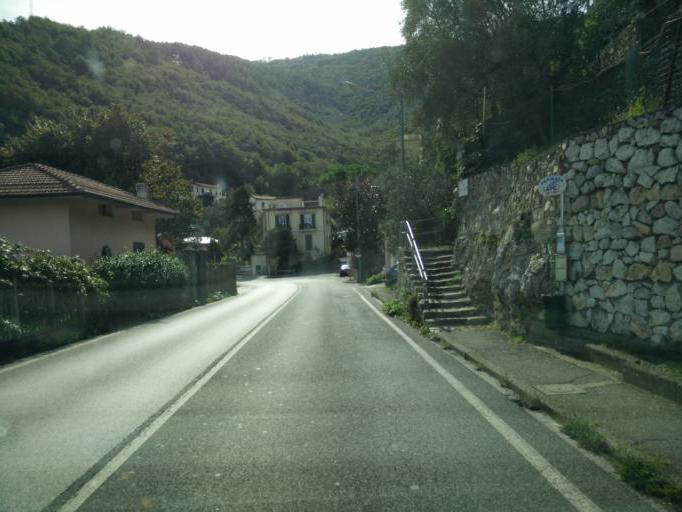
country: IT
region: Liguria
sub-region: Provincia di La Spezia
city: Le Grazie
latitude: 44.0802
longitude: 9.8213
